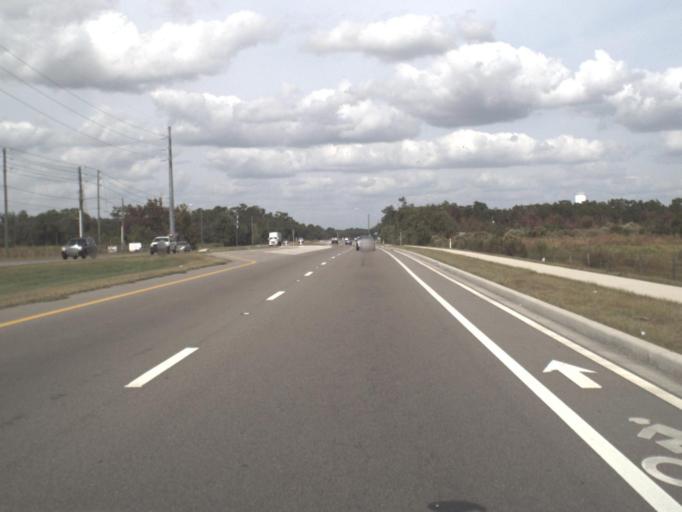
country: US
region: Florida
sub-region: Osceola County
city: Campbell
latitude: 28.2400
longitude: -81.4872
